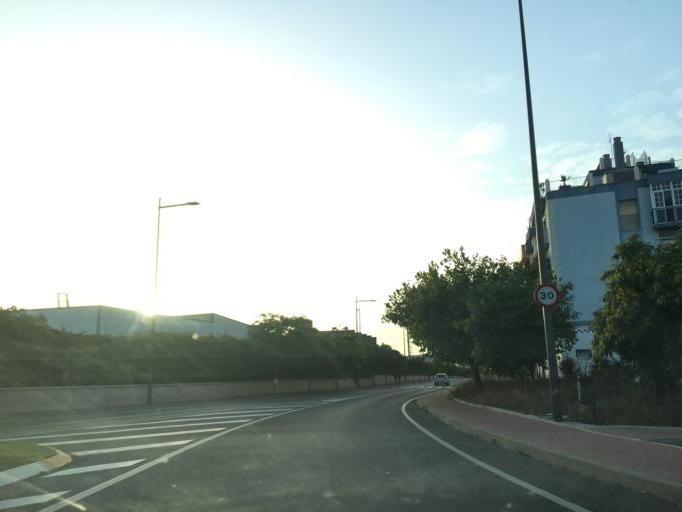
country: ES
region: Murcia
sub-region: Murcia
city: Cartagena
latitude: 37.5953
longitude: -0.9704
